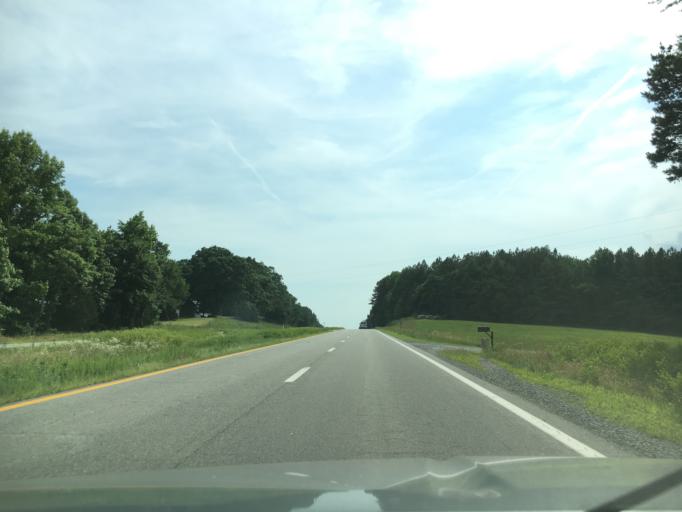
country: US
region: Virginia
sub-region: Mecklenburg County
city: Chase City
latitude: 36.8579
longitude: -78.6008
